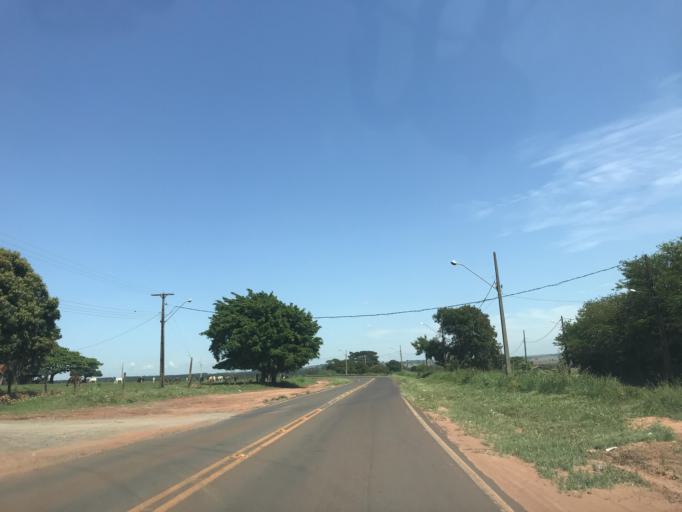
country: BR
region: Parana
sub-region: Paranavai
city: Nova Aurora
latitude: -22.9439
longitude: -52.6937
